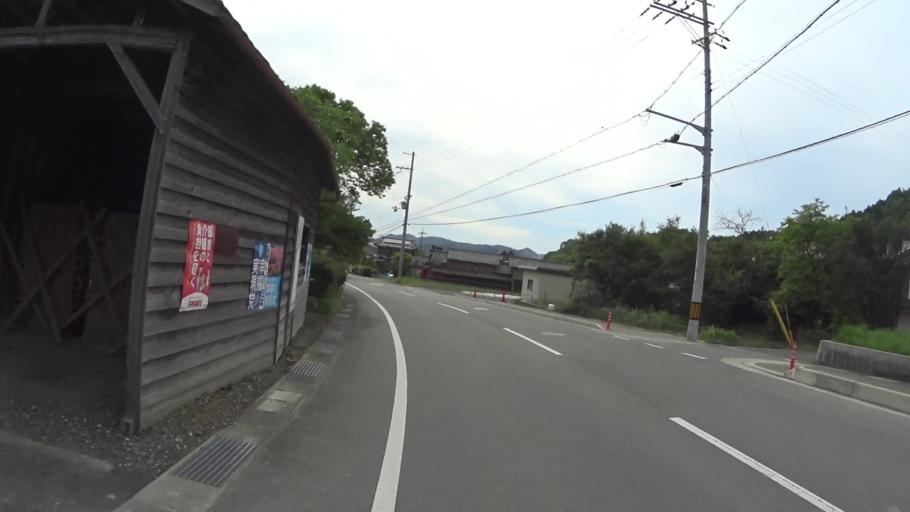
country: JP
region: Kyoto
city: Kameoka
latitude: 35.0974
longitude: 135.5467
